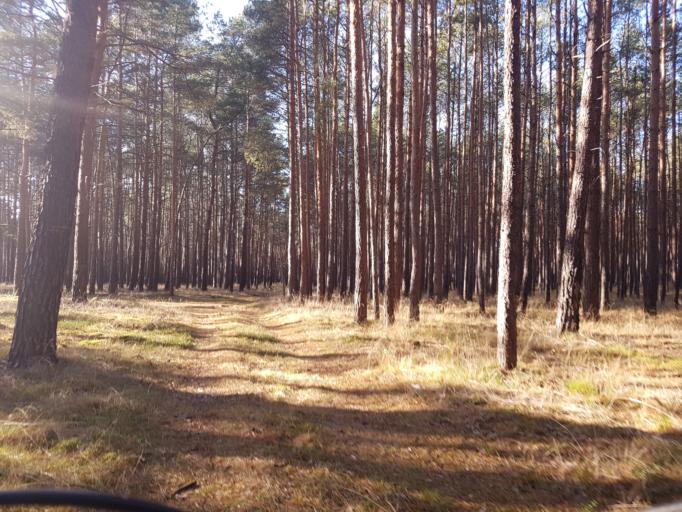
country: DE
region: Brandenburg
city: Schilda
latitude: 51.6192
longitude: 13.3747
